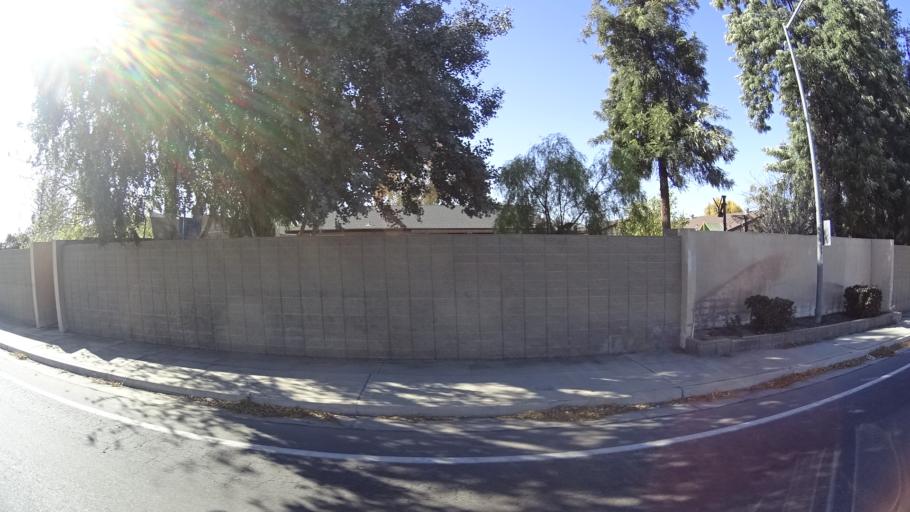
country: US
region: California
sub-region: Kern County
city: Bakersfield
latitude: 35.3313
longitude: -119.0578
